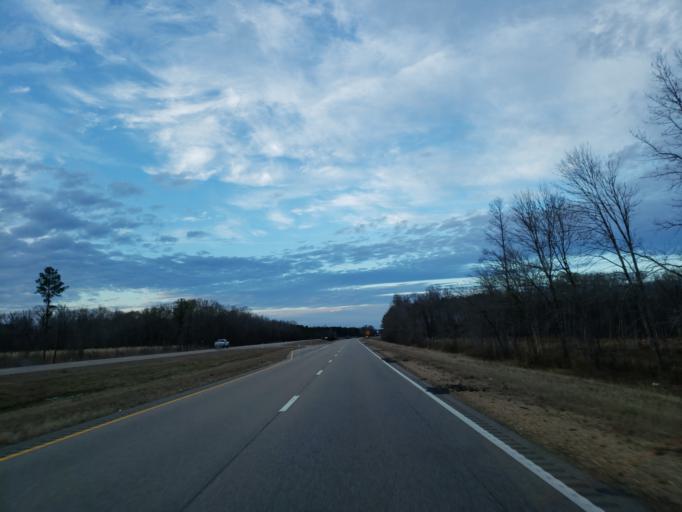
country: US
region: Mississippi
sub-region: Kemper County
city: De Kalb
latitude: 32.7531
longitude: -88.4658
